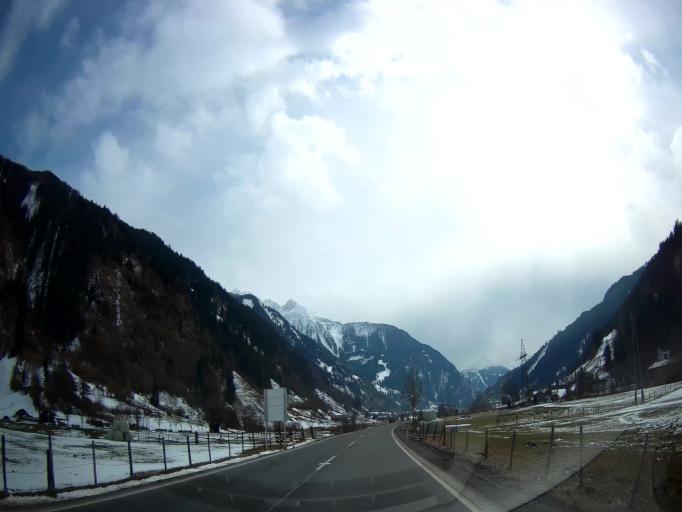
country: AT
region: Salzburg
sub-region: Politischer Bezirk Sankt Johann im Pongau
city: Dorfgastein
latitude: 47.2365
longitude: 13.1058
